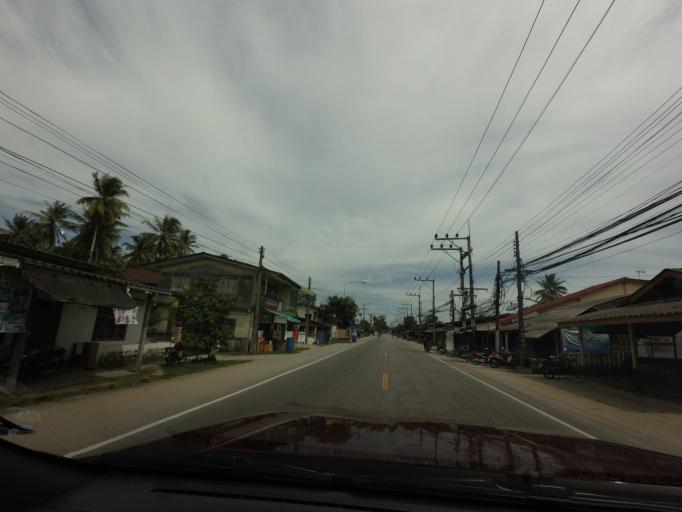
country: TH
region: Narathiwat
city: Tak Bai
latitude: 6.2554
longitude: 102.0591
